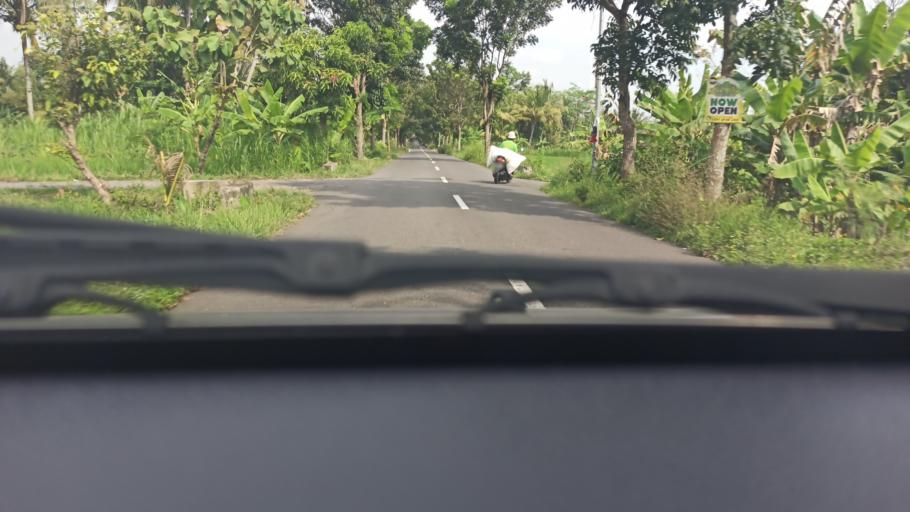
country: ID
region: Daerah Istimewa Yogyakarta
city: Sleman
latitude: -7.7013
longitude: 110.2984
